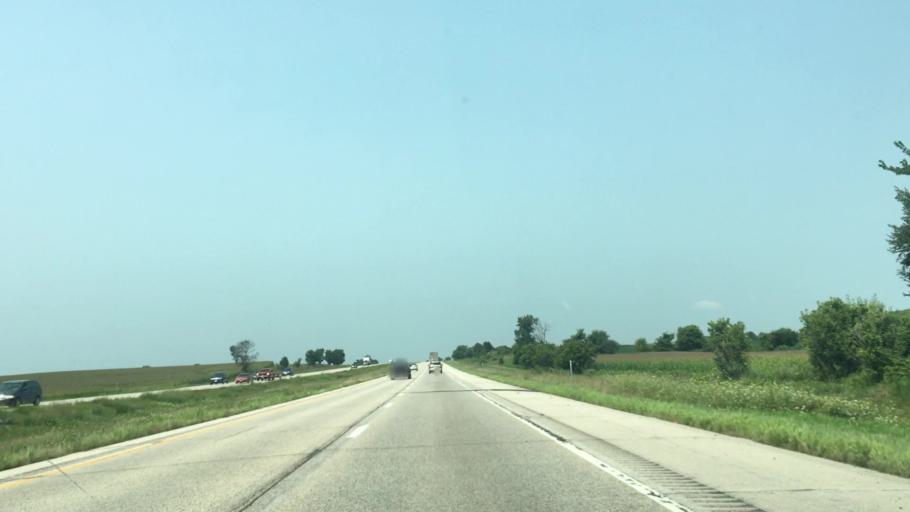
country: US
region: Iowa
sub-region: Linn County
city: Center Point
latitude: 42.1480
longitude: -91.7459
